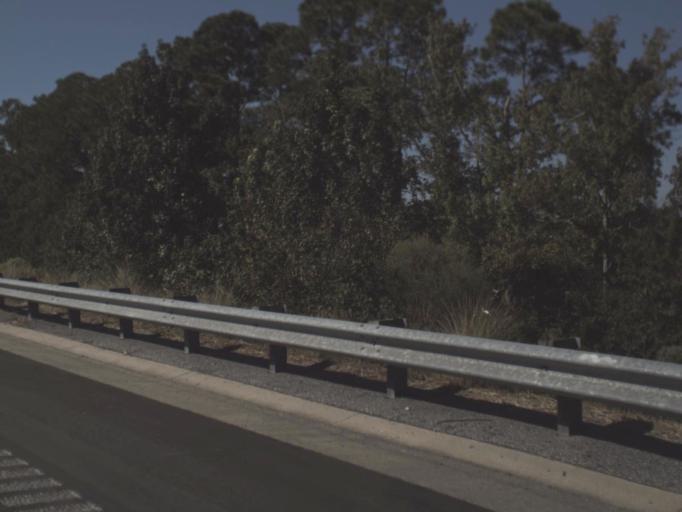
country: US
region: Florida
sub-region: Seminole County
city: Lake Mary
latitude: 28.8000
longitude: -81.3148
